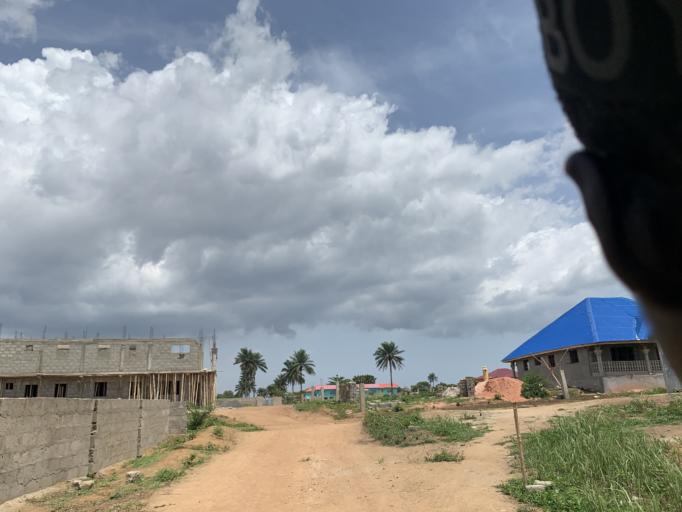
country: SL
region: Western Area
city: Waterloo
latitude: 8.3400
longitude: -13.0361
